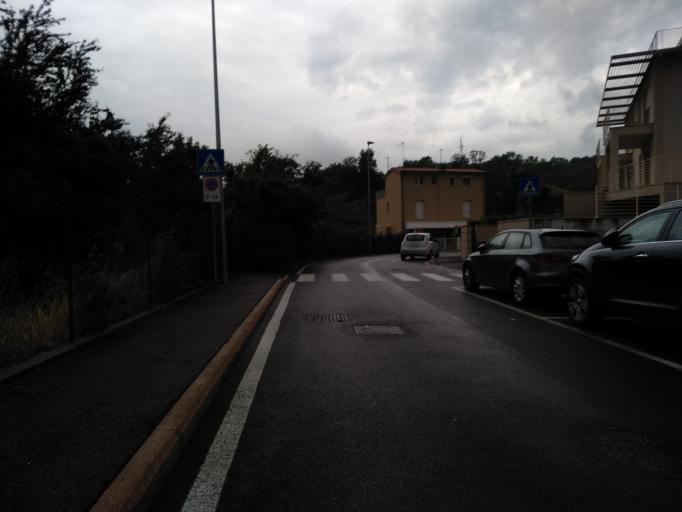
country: IT
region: Tuscany
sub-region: Province of Arezzo
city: San Giovanni Valdarno
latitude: 43.5619
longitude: 11.5278
